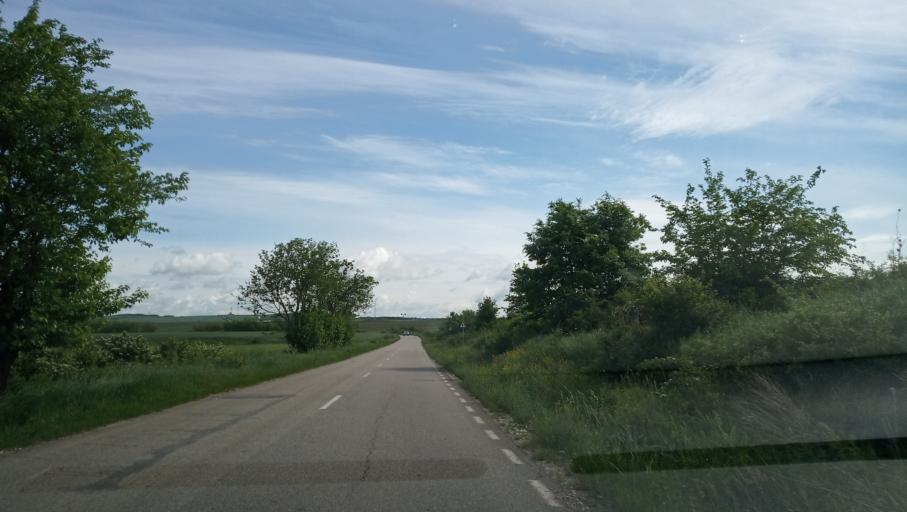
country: RO
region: Timis
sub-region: Comuna Topolovatu Mare
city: Topolovatu Mare
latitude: 45.7896
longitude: 21.6519
